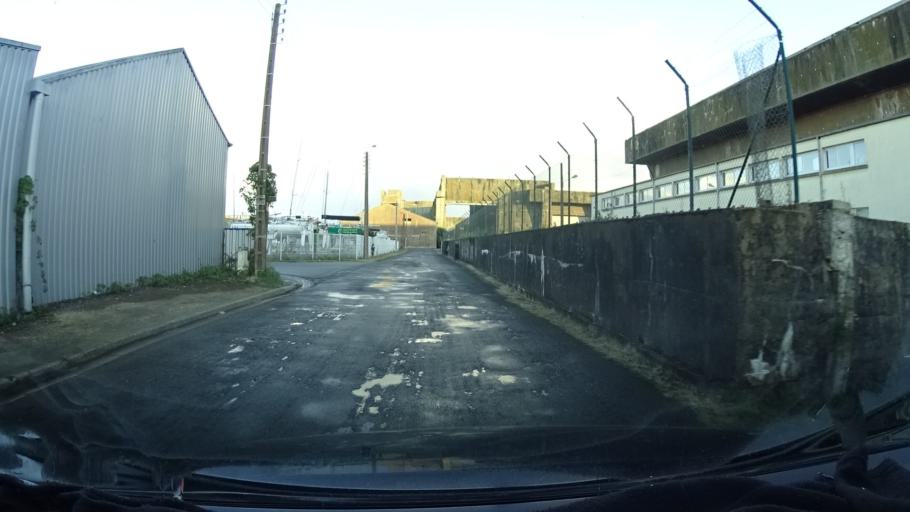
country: FR
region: Brittany
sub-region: Departement du Morbihan
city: Lorient
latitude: 47.7315
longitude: -3.3709
